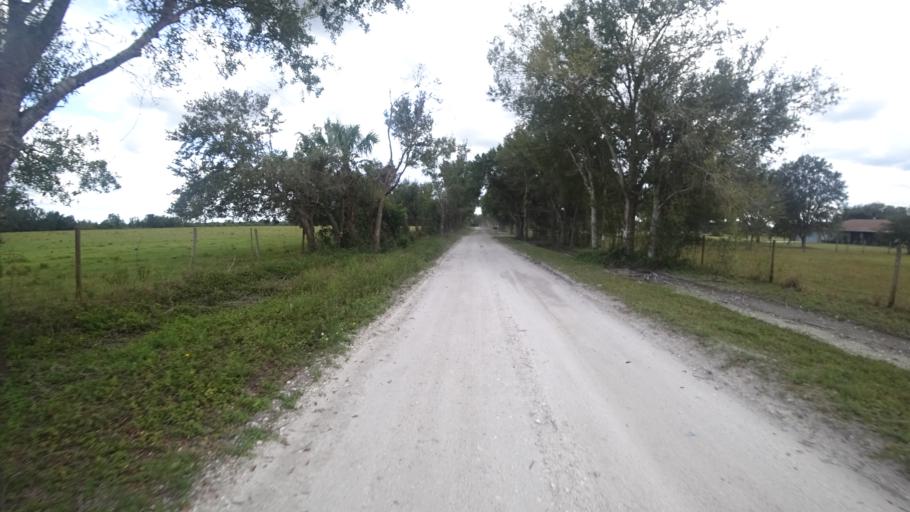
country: US
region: Florida
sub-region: Sarasota County
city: Lake Sarasota
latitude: 27.3971
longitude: -82.2663
